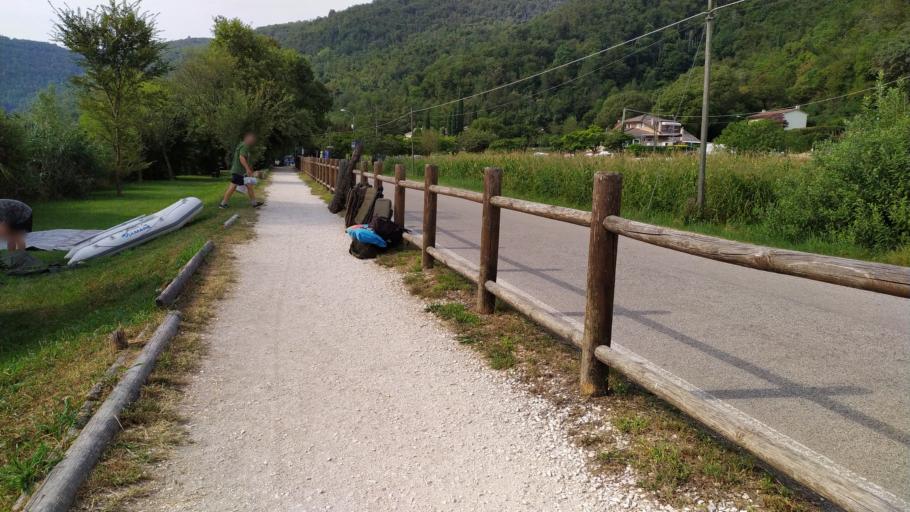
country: IT
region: Veneto
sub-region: Provincia di Vicenza
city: Arcugnano-Torri
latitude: 45.4712
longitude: 11.5408
